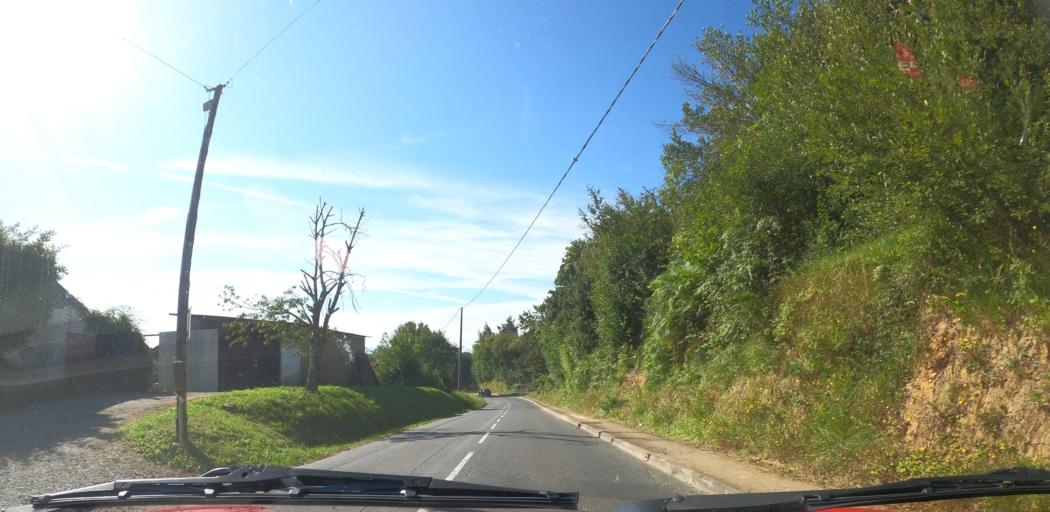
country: FR
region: Aquitaine
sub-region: Departement des Pyrenees-Atlantiques
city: Arbonne
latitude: 43.4169
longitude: -1.5488
